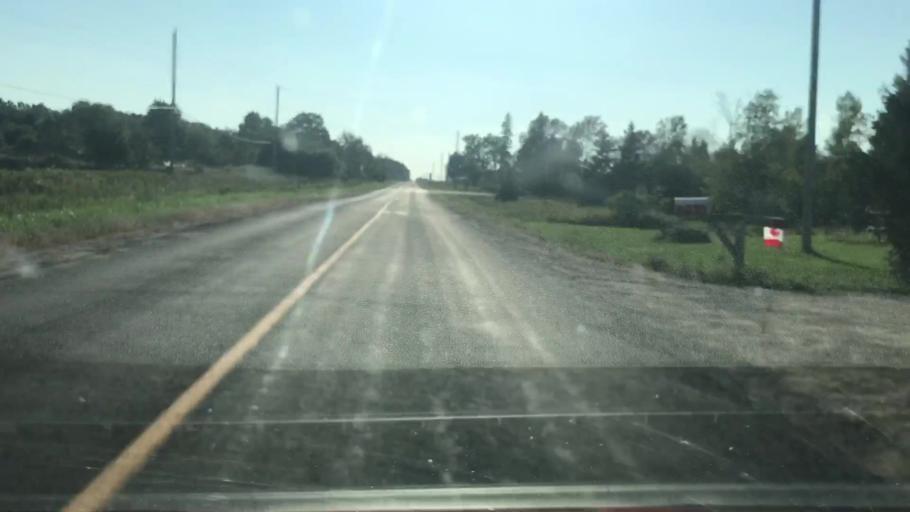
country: US
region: Michigan
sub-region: Chippewa County
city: Sault Ste. Marie
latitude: 46.2860
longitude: -84.0543
